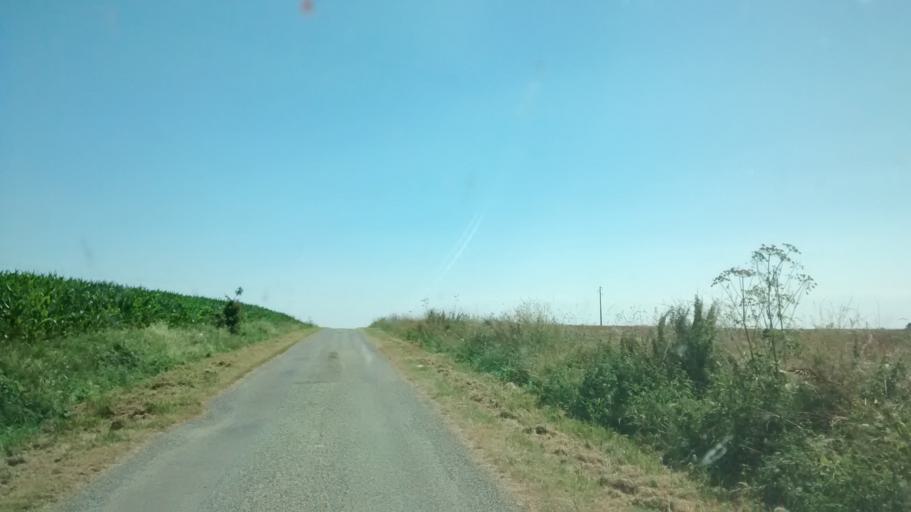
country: FR
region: Brittany
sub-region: Departement d'Ille-et-Vilaine
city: Chantepie
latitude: 48.0950
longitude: -1.5913
